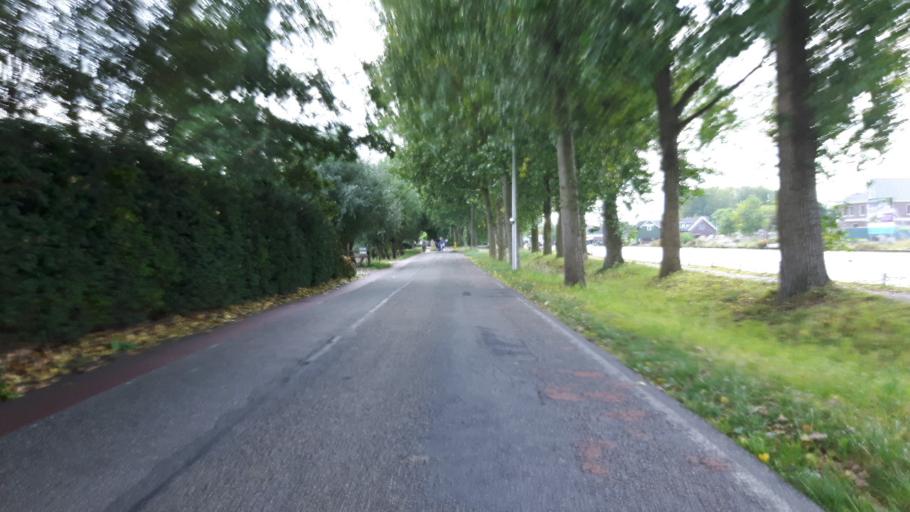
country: NL
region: South Holland
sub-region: Bodegraven-Reeuwijk
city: Bodegraven
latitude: 52.0941
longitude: 4.7389
